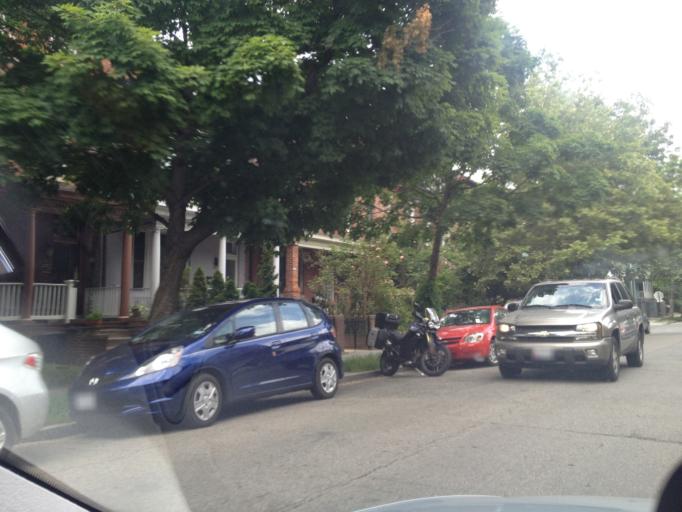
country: US
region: Washington, D.C.
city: Washington, D.C.
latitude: 38.9318
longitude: -77.0314
